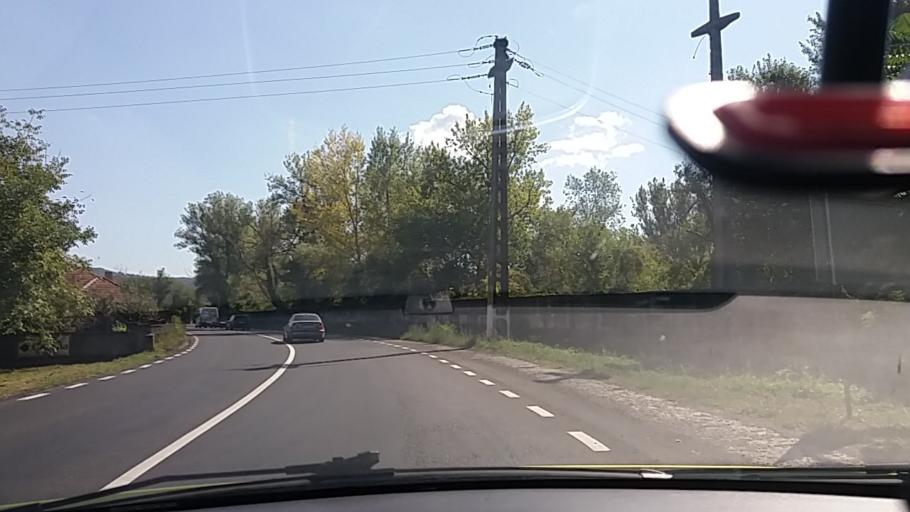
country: RO
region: Hunedoara
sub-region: Comuna Ilia
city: Ilia
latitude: 45.9339
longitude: 22.6524
